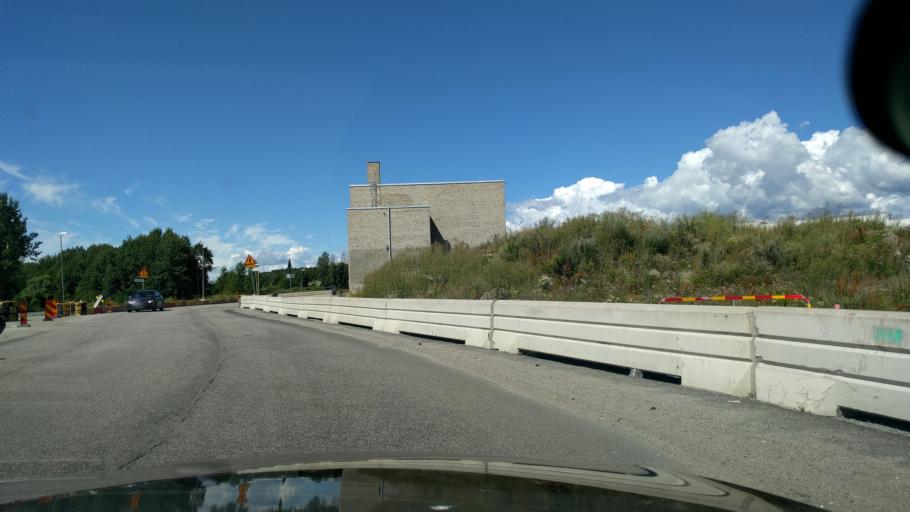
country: SE
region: Stockholm
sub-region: Jarfalla Kommun
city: Jakobsberg
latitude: 59.4095
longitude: 17.8645
